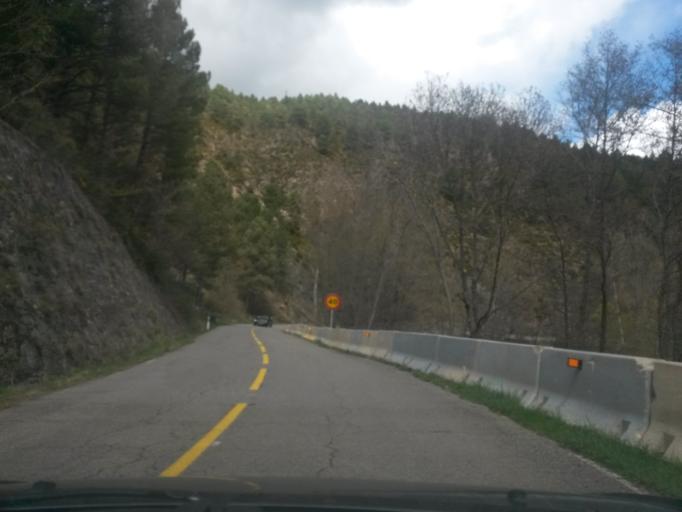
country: ES
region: Catalonia
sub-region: Provincia de Lleida
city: Lles de Cerdanya
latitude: 42.3663
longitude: 1.7108
